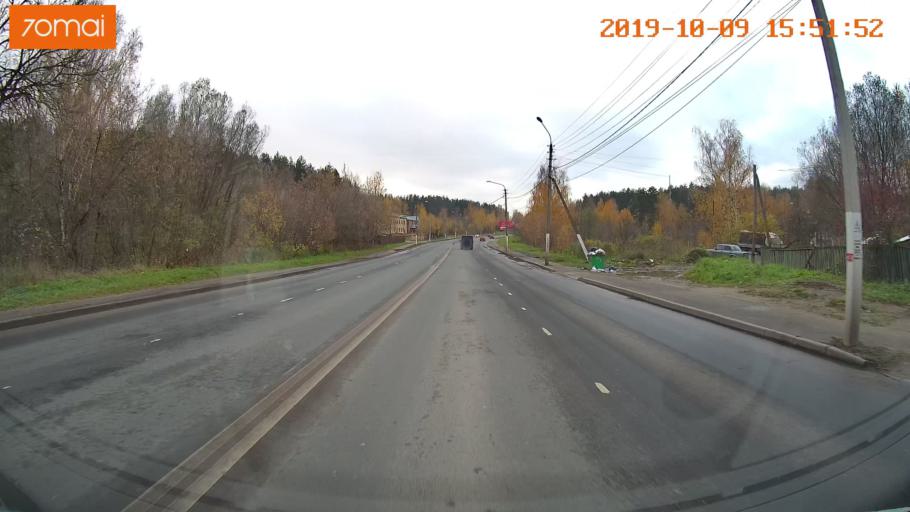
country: RU
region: Kostroma
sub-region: Kostromskoy Rayon
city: Kostroma
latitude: 57.7941
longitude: 40.9749
